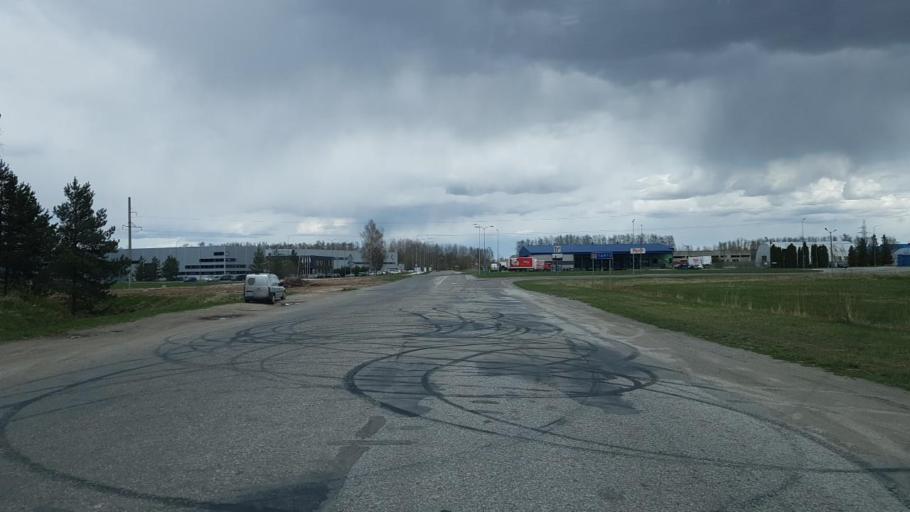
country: EE
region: Tartu
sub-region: Tartu linn
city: Tartu
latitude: 58.3893
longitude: 26.6755
